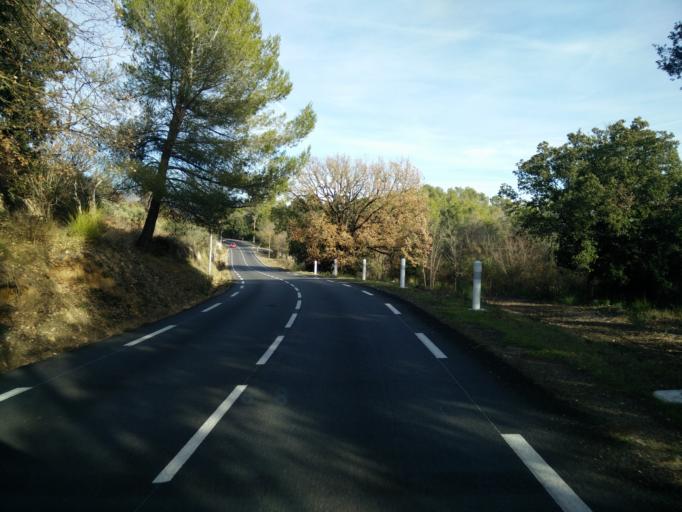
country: FR
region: Provence-Alpes-Cote d'Azur
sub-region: Departement du Var
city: Montauroux
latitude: 43.5976
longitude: 6.7998
